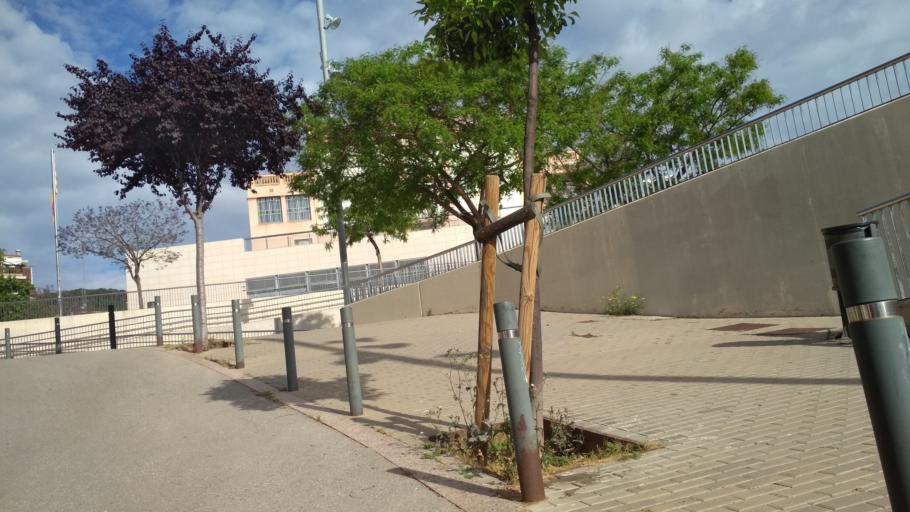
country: ES
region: Catalonia
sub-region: Provincia de Barcelona
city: Horta-Guinardo
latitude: 41.4181
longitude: 2.1755
